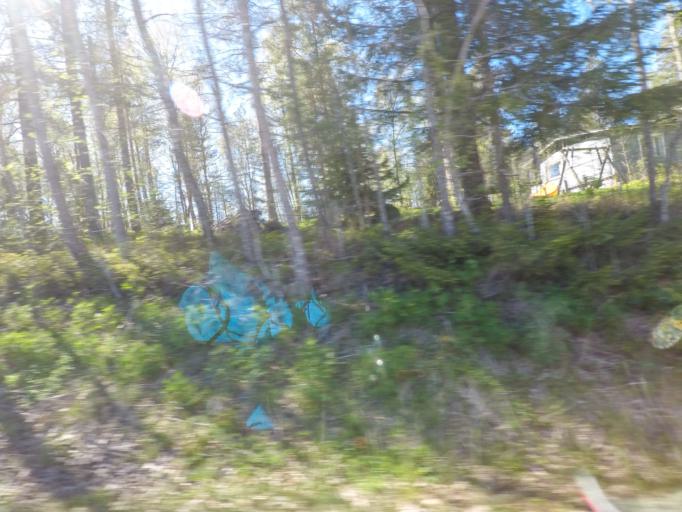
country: FI
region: Uusimaa
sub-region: Helsinki
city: Sammatti
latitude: 60.3466
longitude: 23.8006
